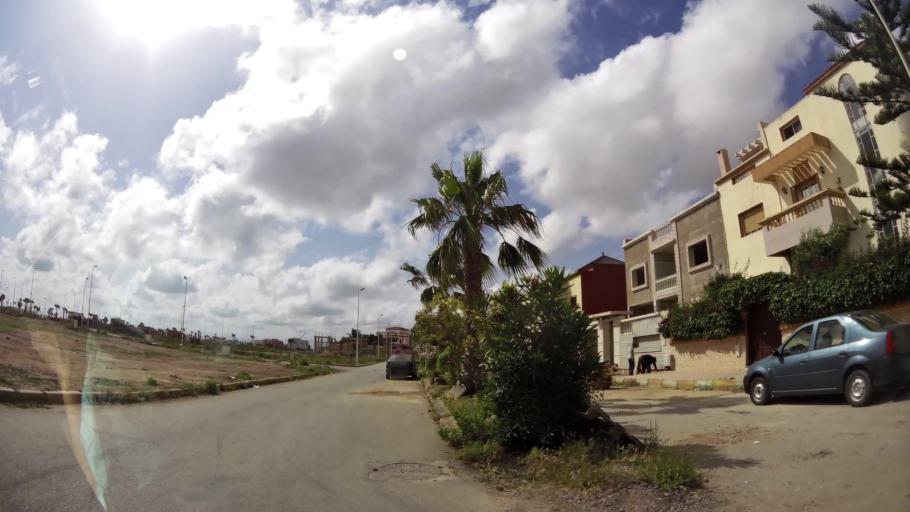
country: MA
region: Oriental
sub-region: Nador
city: Nador
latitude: 35.1665
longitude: -2.9146
